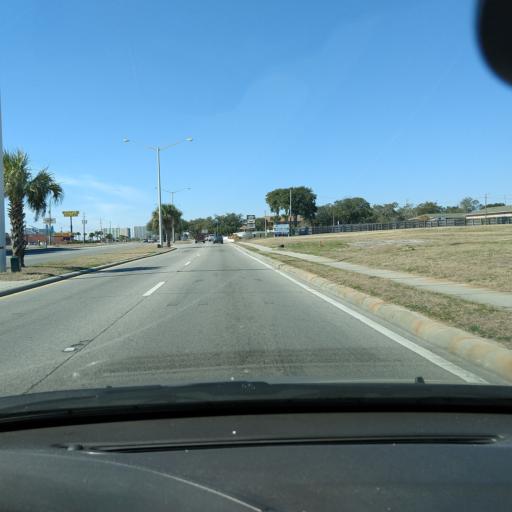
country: US
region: Mississippi
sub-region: Harrison County
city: Biloxi
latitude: 30.3937
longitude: -88.9402
